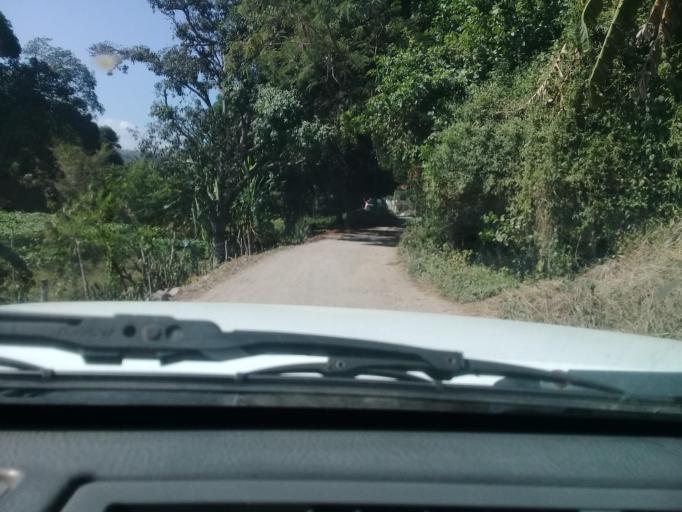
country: MX
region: Veracruz
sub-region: Emiliano Zapata
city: Plan del Rio
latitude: 19.4259
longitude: -96.6143
